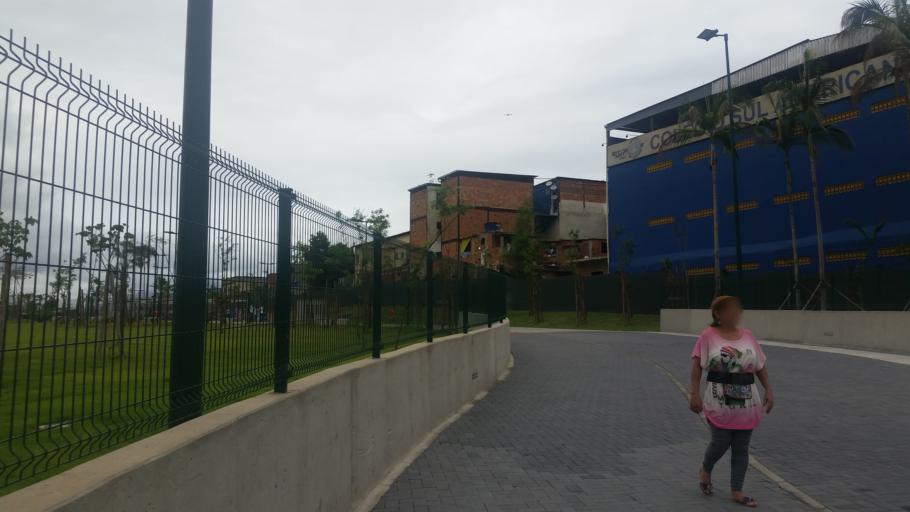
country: BR
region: Rio de Janeiro
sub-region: Sao Joao De Meriti
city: Sao Joao de Meriti
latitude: -22.8497
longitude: -43.3582
